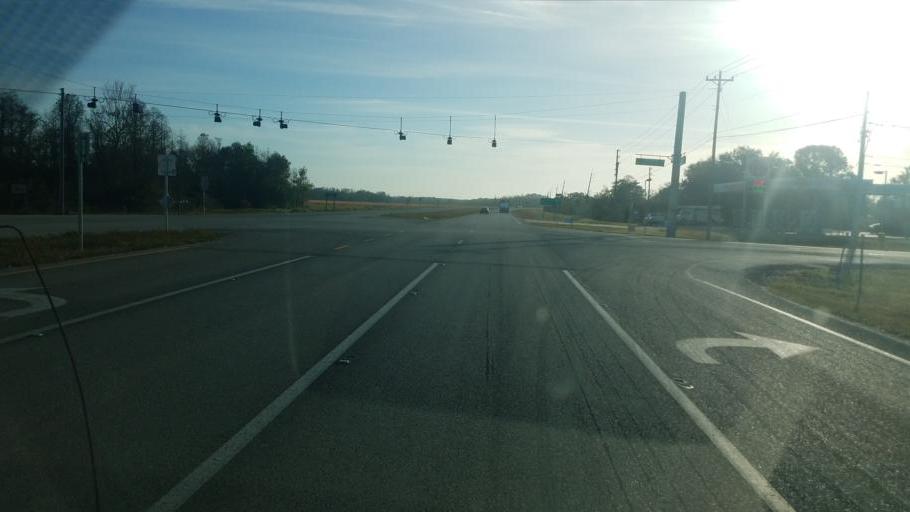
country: US
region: Florida
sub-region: Osceola County
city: Saint Cloud
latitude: 28.1448
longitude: -81.0767
